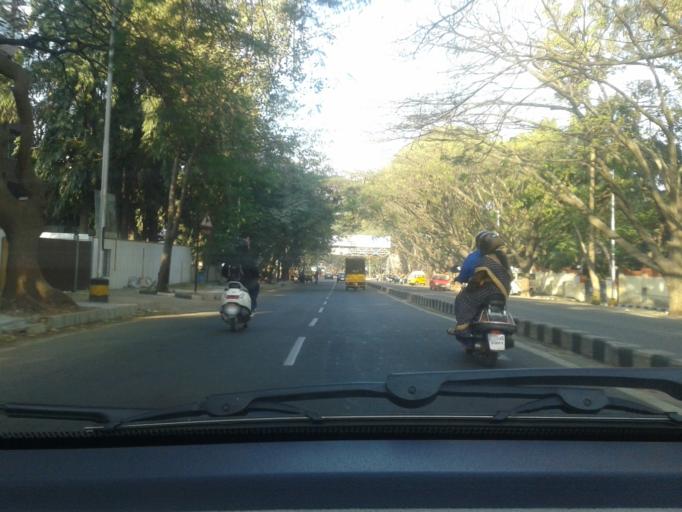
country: IN
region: Karnataka
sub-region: Bangalore Urban
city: Bangalore
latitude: 13.0147
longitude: 77.5770
